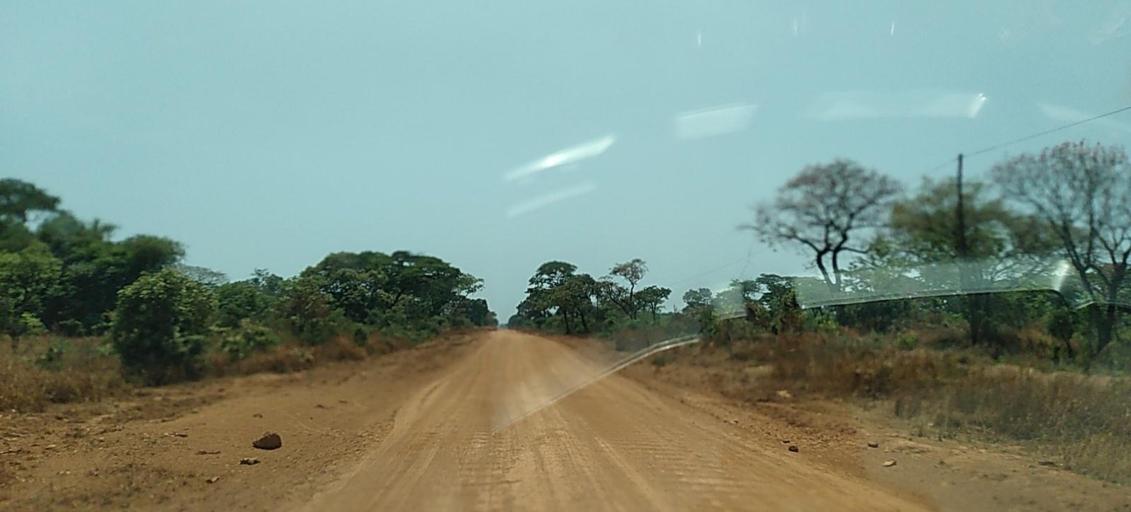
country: CD
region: Katanga
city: Kipushi
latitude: -11.9307
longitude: 26.9828
